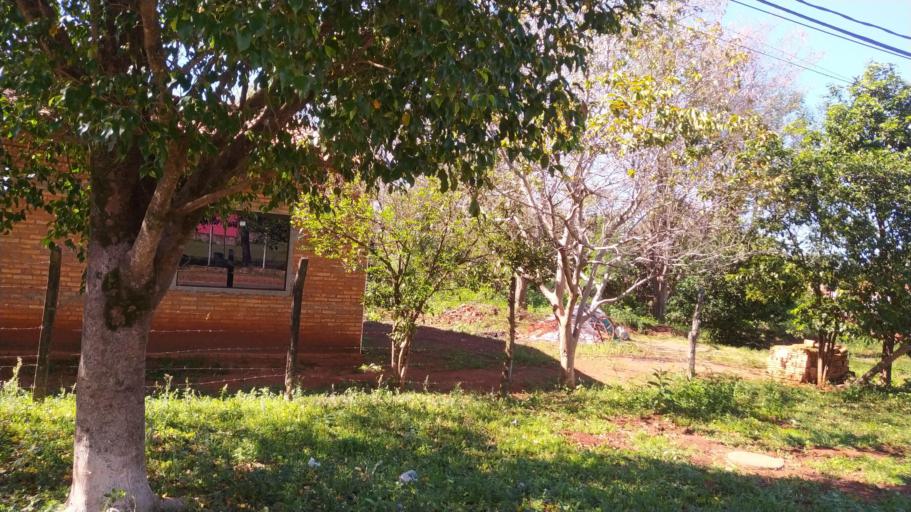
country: PY
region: Misiones
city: San Juan Bautista
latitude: -26.6729
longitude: -57.1379
